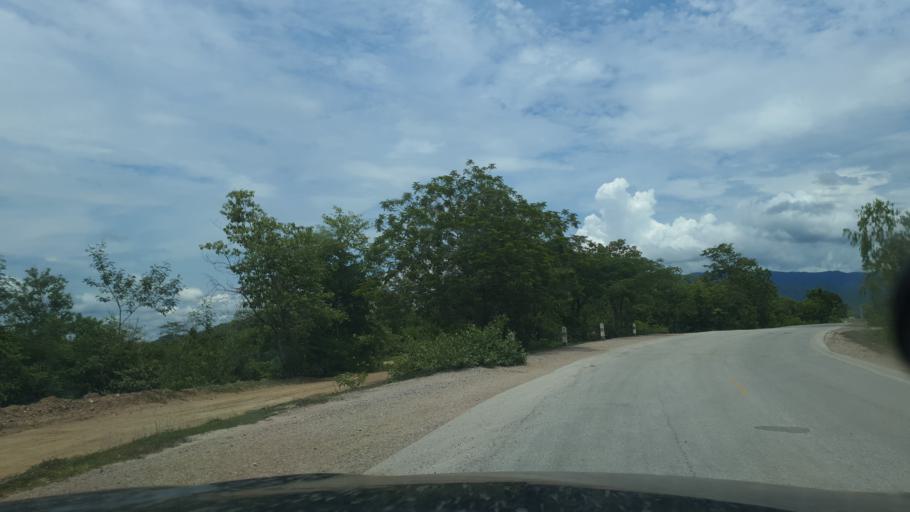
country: TH
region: Lampang
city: Sop Prap
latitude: 17.9339
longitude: 99.3654
